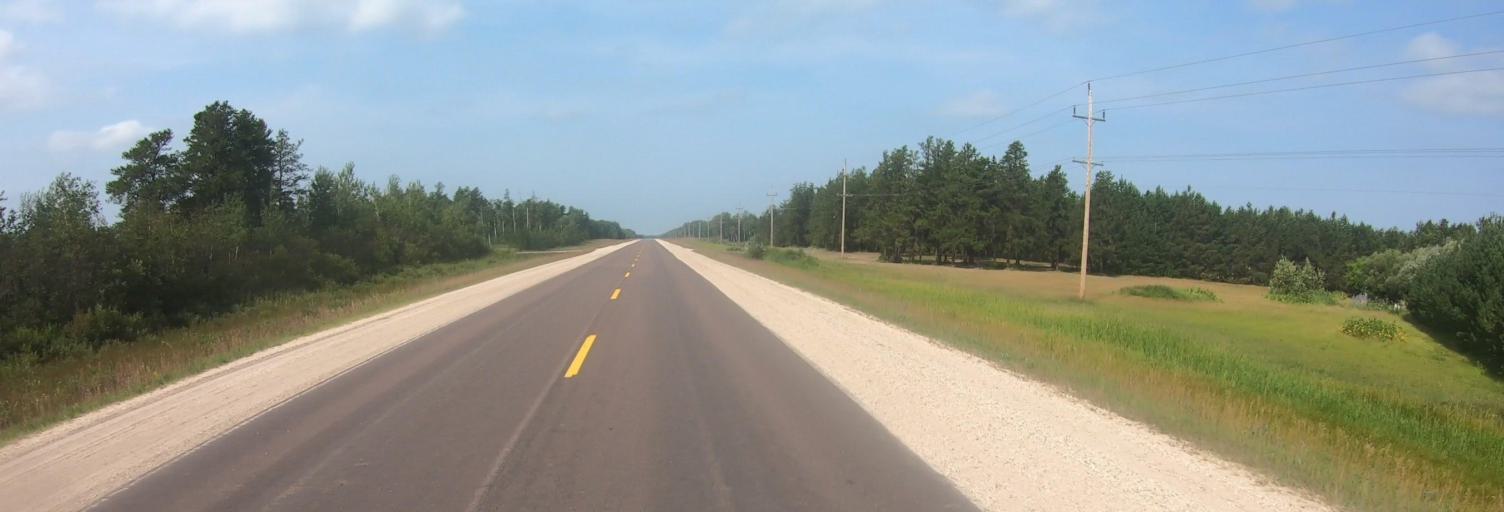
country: CA
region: Manitoba
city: La Broquerie
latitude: 49.2669
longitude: -96.4269
